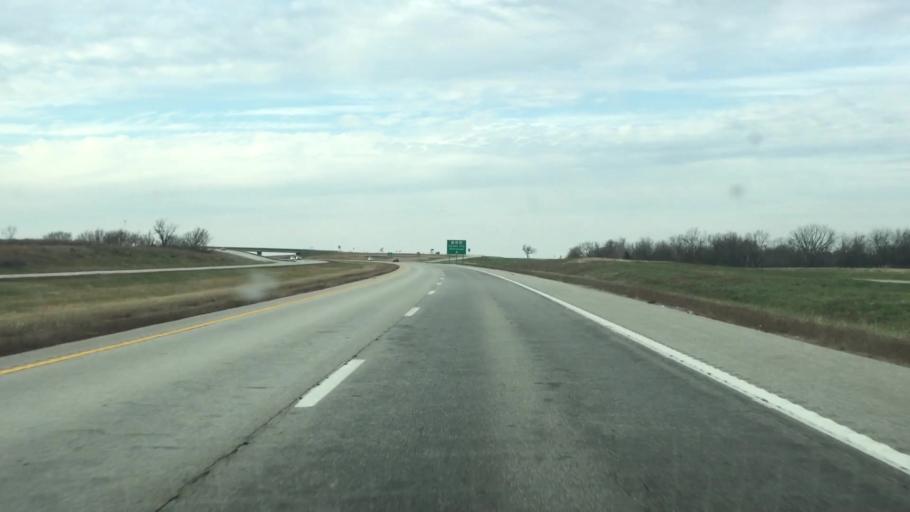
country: US
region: Missouri
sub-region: Cass County
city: Garden City
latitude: 38.5681
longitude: -94.1875
